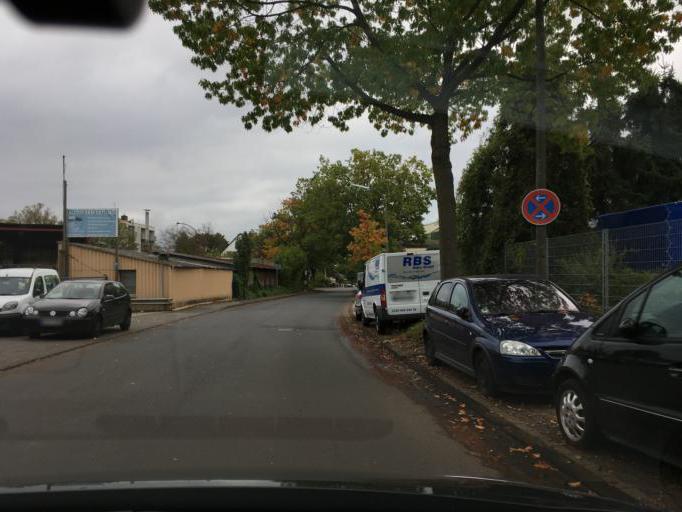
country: DE
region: North Rhine-Westphalia
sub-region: Regierungsbezirk Koln
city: Bonn
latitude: 50.7337
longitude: 7.1433
